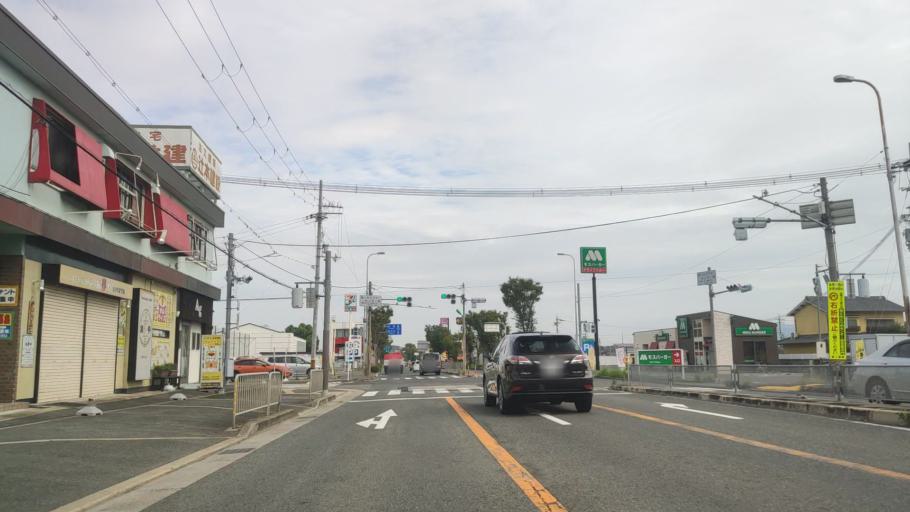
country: JP
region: Osaka
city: Tondabayashicho
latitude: 34.5351
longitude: 135.6047
